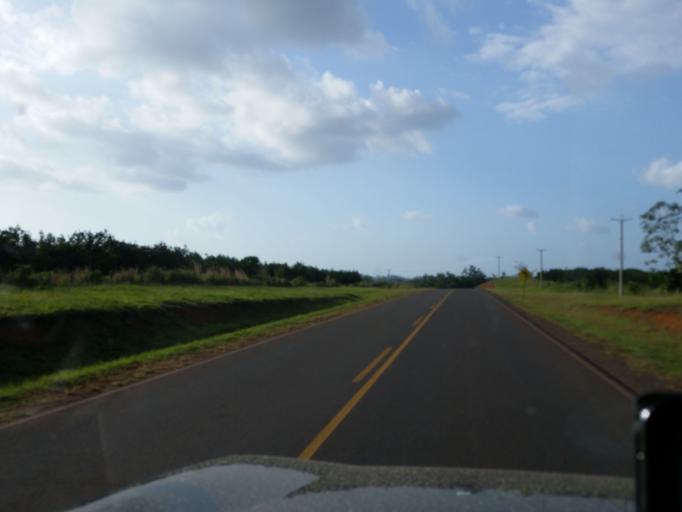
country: NI
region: Rio San Juan
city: San Carlos
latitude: 11.1646
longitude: -84.6645
